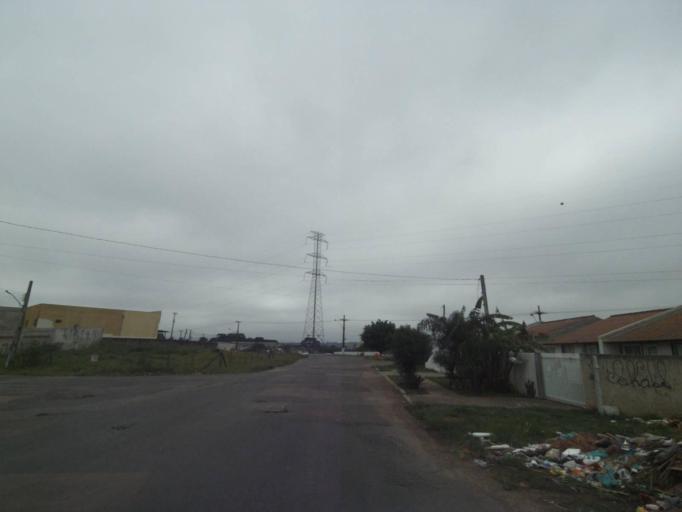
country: BR
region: Parana
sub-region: Curitiba
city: Curitiba
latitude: -25.4934
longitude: -49.3449
